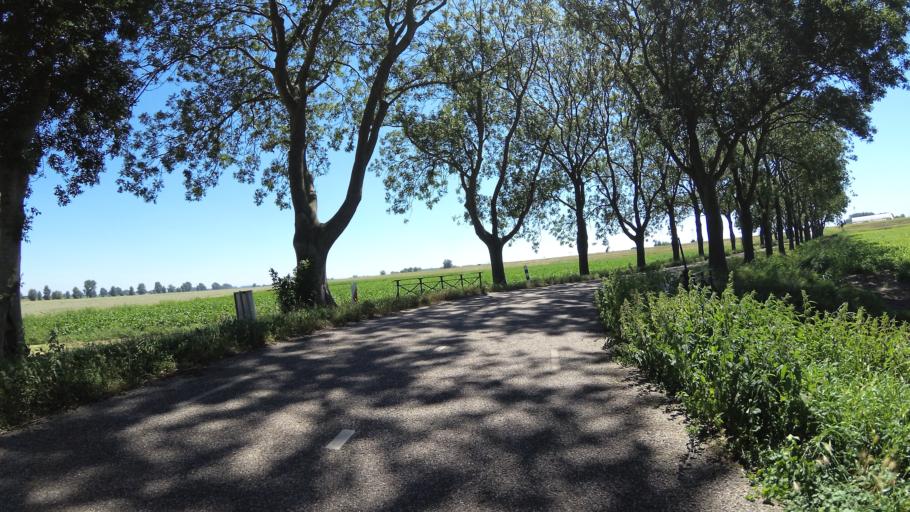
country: NL
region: North Brabant
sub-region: Gemeente Waalwijk
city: Waspik
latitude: 51.7138
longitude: 4.9839
